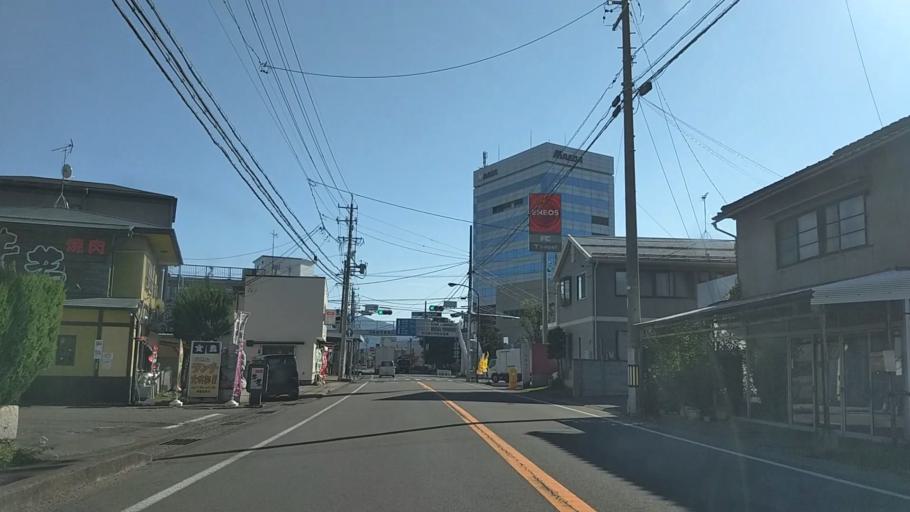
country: JP
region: Nagano
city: Nagano-shi
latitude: 36.5733
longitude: 138.1429
